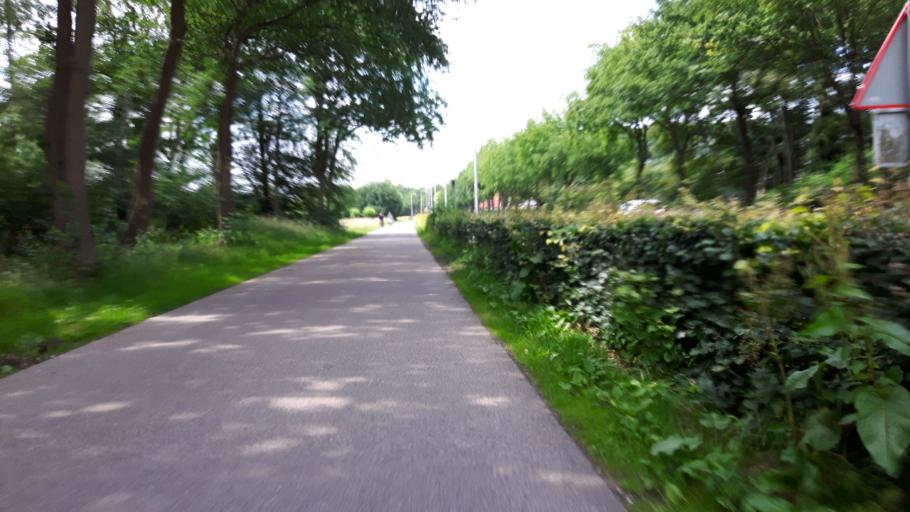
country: NL
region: Utrecht
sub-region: Gemeente De Bilt
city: De Bilt
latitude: 52.1394
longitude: 5.1871
